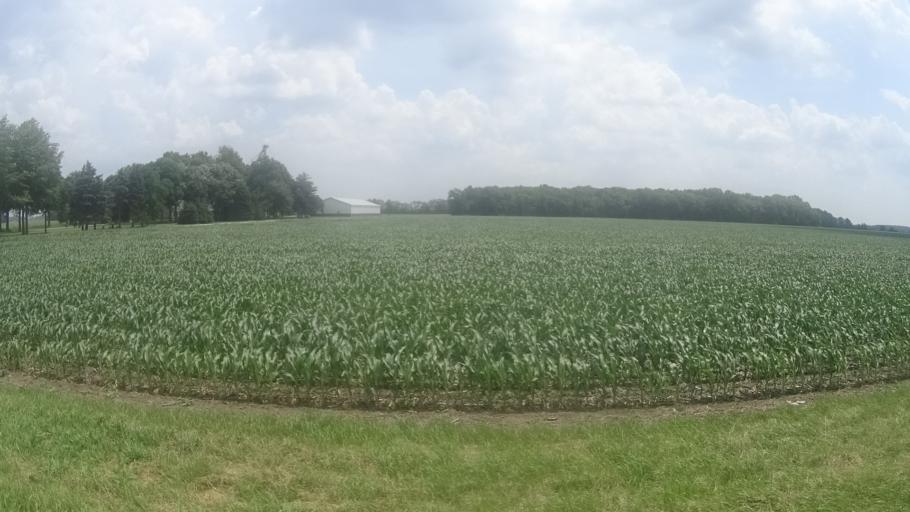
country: US
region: Ohio
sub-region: Huron County
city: Monroeville
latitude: 41.3186
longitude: -82.6930
